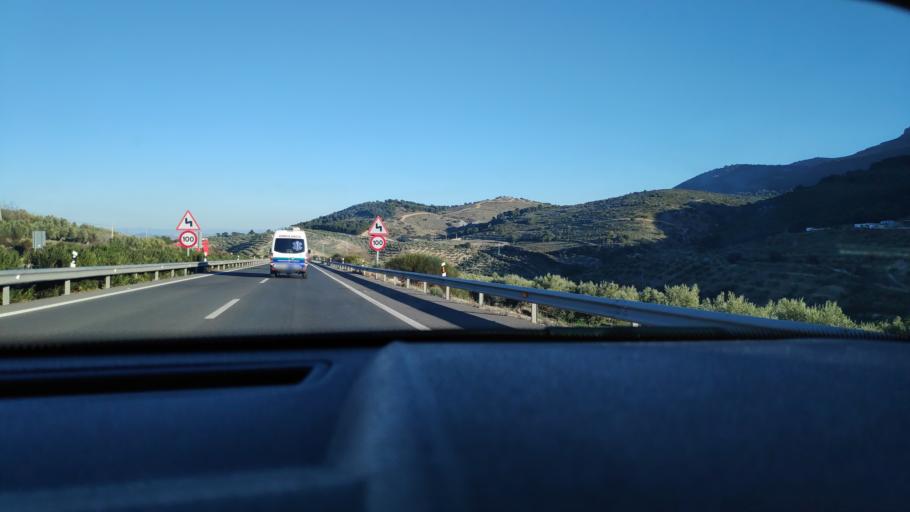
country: ES
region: Andalusia
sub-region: Provincia de Jaen
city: Torre del Campo
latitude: 37.7810
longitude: -3.8607
